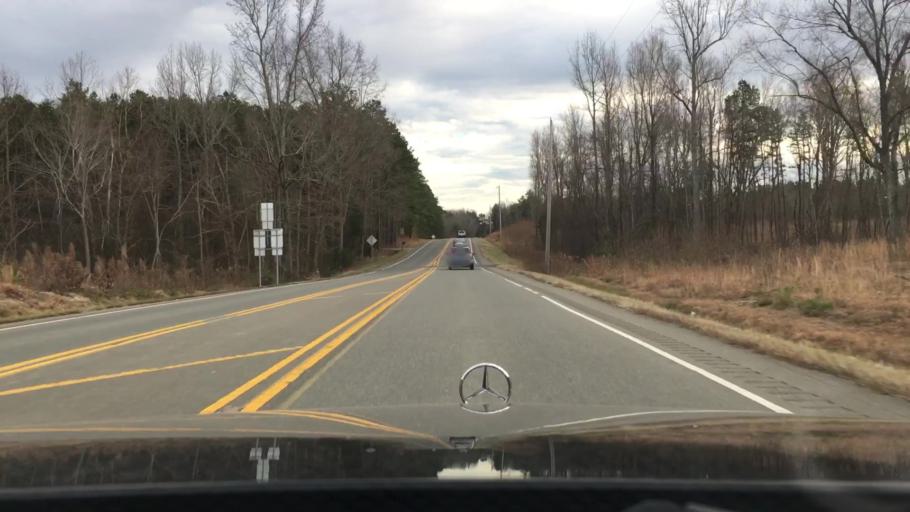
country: US
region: North Carolina
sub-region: Alamance County
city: Mebane
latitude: 36.2382
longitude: -79.1899
